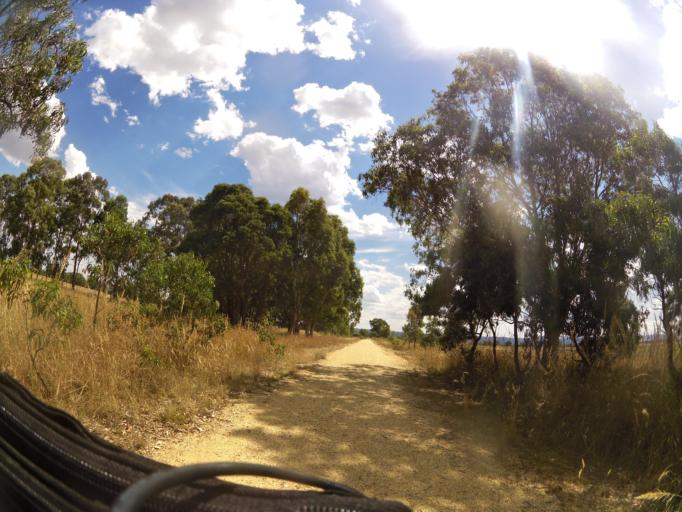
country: AU
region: Victoria
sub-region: Wellington
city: Heyfield
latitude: -37.9766
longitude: 146.7587
